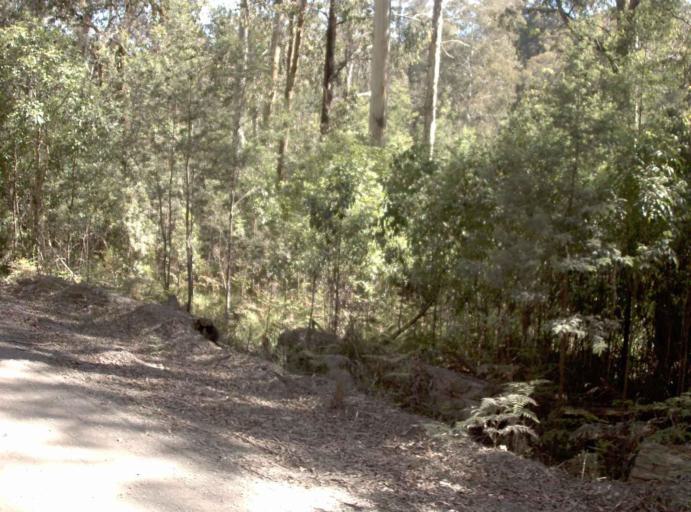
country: AU
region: New South Wales
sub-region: Bombala
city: Bombala
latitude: -37.2288
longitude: 148.7514
